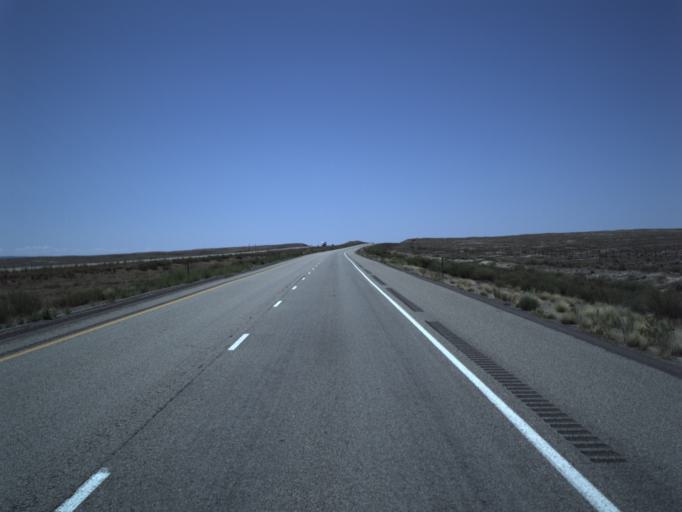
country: US
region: Utah
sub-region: Grand County
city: Moab
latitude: 39.0139
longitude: -109.3052
